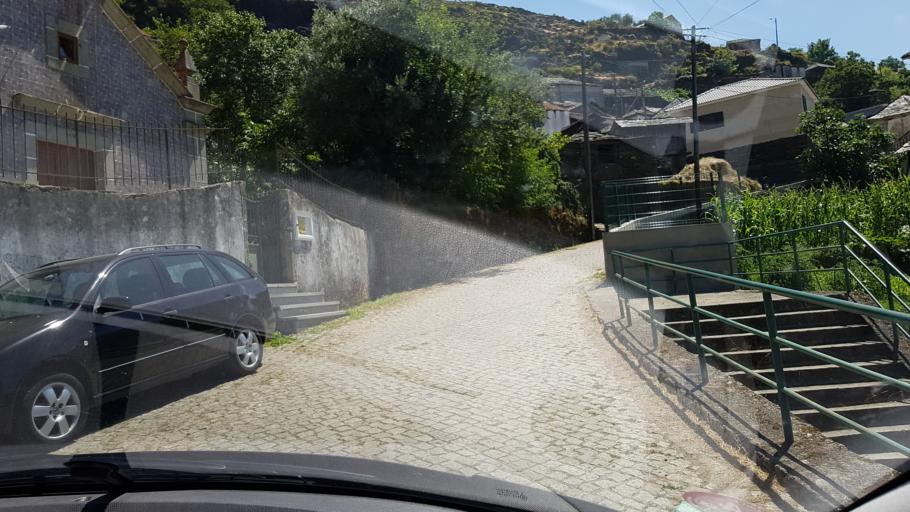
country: PT
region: Vila Real
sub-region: Mondim de Basto
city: Mondim de Basto
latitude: 41.3356
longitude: -7.8924
